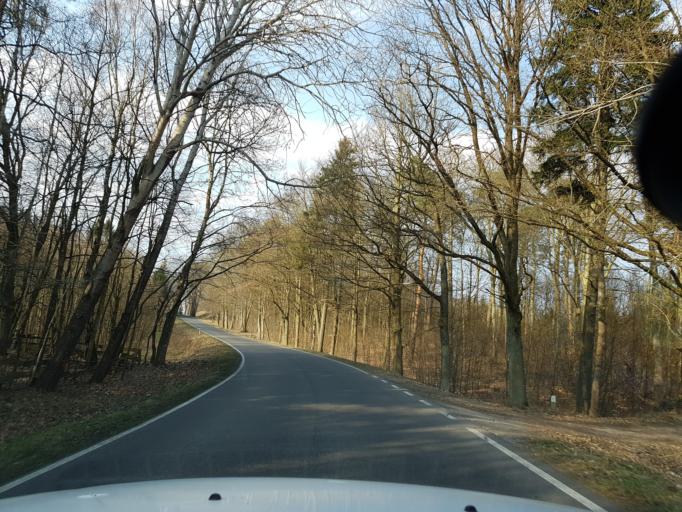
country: PL
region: West Pomeranian Voivodeship
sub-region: Powiat drawski
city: Zlocieniec
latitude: 53.6155
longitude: 15.9228
